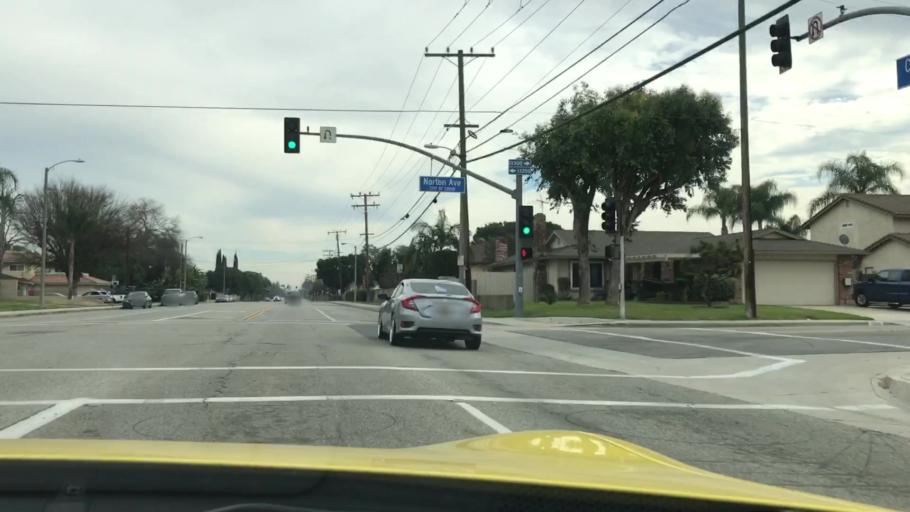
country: US
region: California
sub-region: San Bernardino County
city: Chino
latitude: 34.0116
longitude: -117.7112
